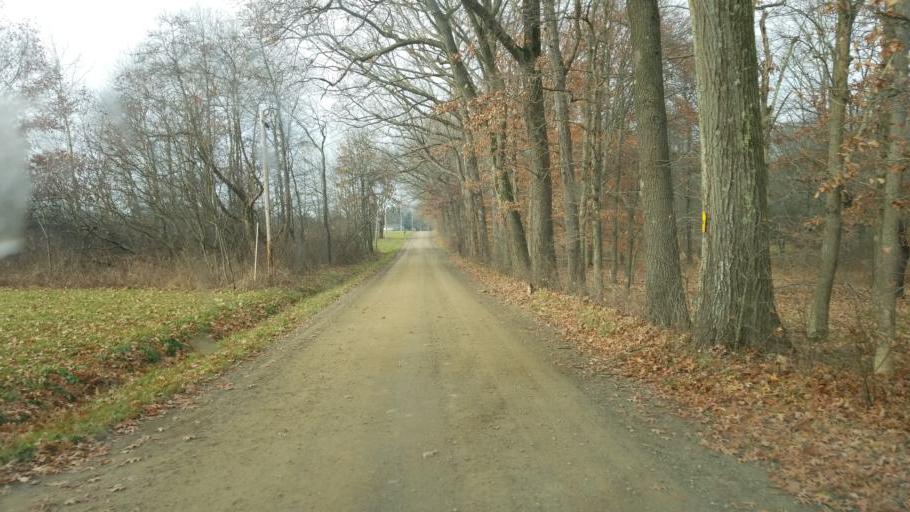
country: US
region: Pennsylvania
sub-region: Crawford County
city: Cochranton
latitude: 41.5201
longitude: -80.1185
